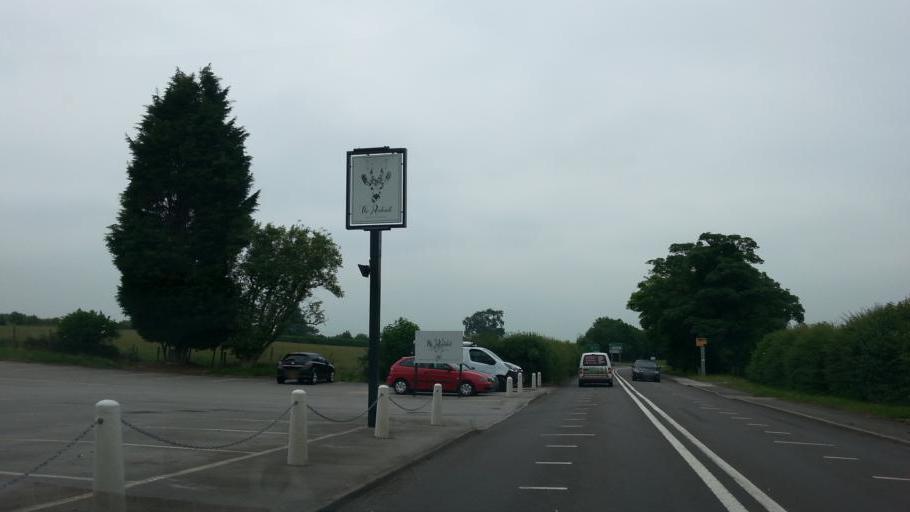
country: GB
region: England
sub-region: Staffordshire
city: Uttoxeter
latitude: 52.8607
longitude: -1.7677
